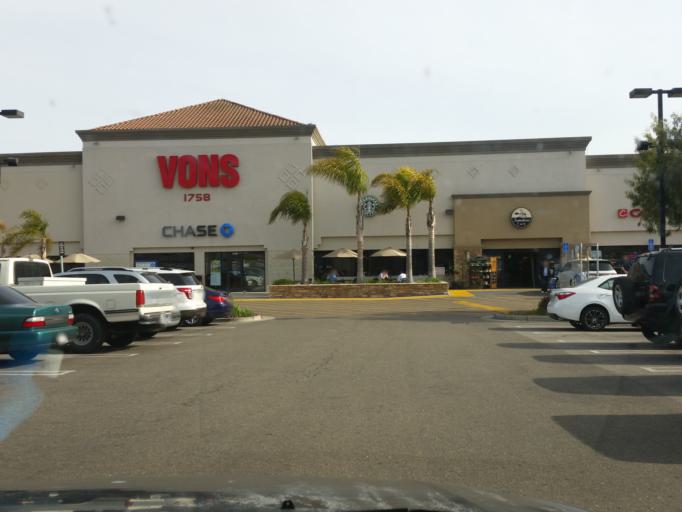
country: US
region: California
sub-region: San Luis Obispo County
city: Grover Beach
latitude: 35.1206
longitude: -120.6104
